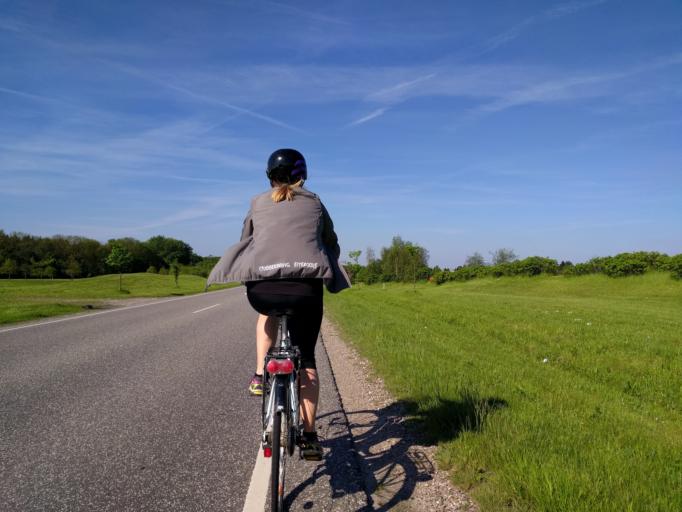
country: DK
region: Zealand
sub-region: Guldborgsund Kommune
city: Nykobing Falster
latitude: 54.7569
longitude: 11.9105
